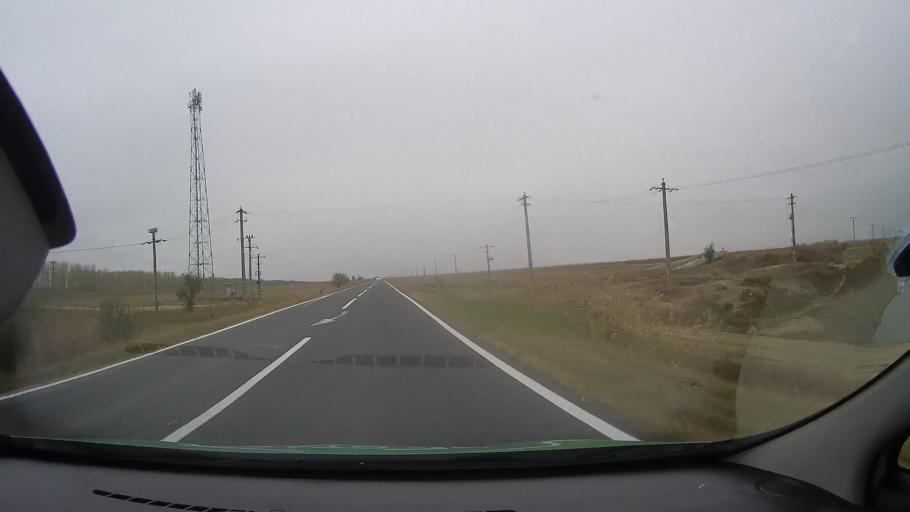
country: RO
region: Ialomita
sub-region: Comuna Giurgeni
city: Giurgeni
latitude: 44.7232
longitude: 27.8531
